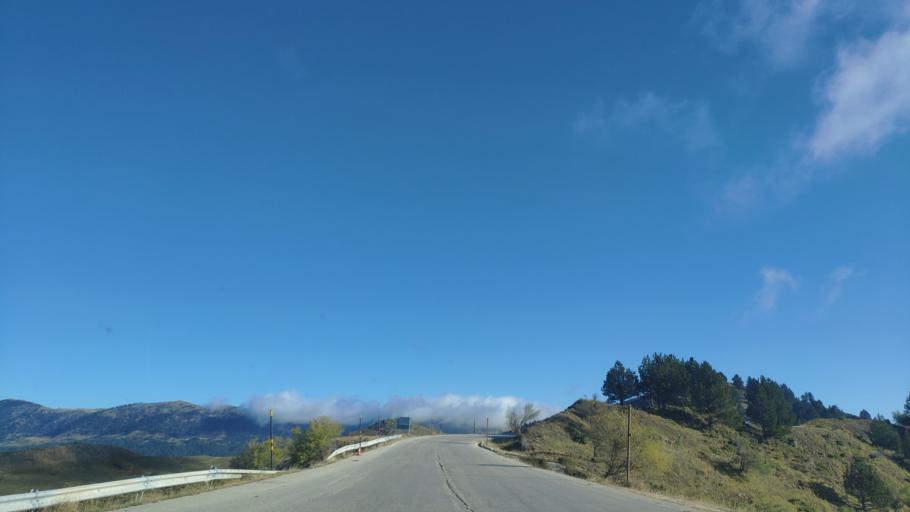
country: GR
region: Epirus
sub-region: Nomos Ioanninon
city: Metsovo
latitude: 39.7926
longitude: 21.1657
